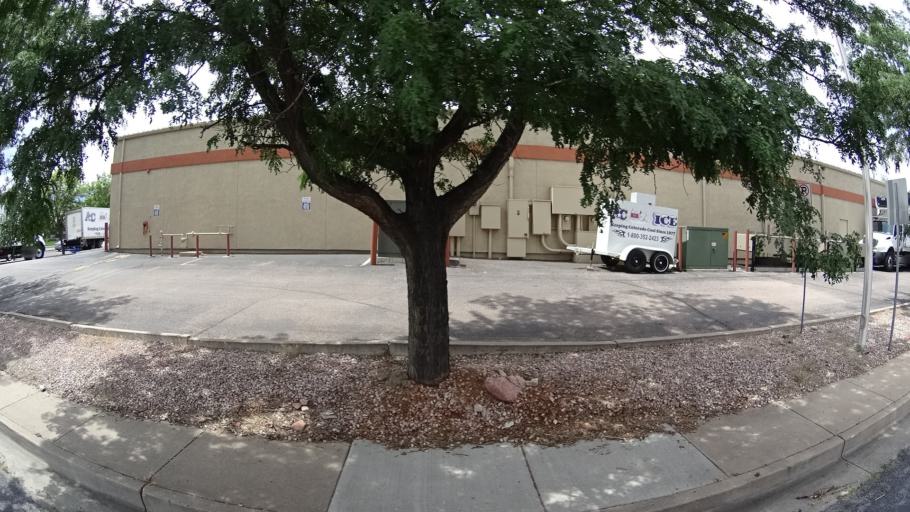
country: US
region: Colorado
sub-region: El Paso County
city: Colorado Springs
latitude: 38.8972
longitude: -104.8411
